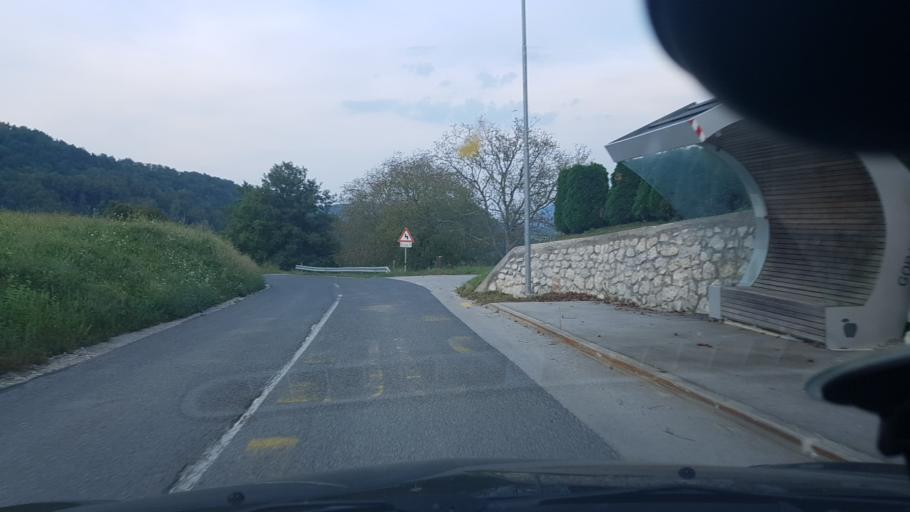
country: SI
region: Kozje
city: Kozje
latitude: 46.0378
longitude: 15.5752
